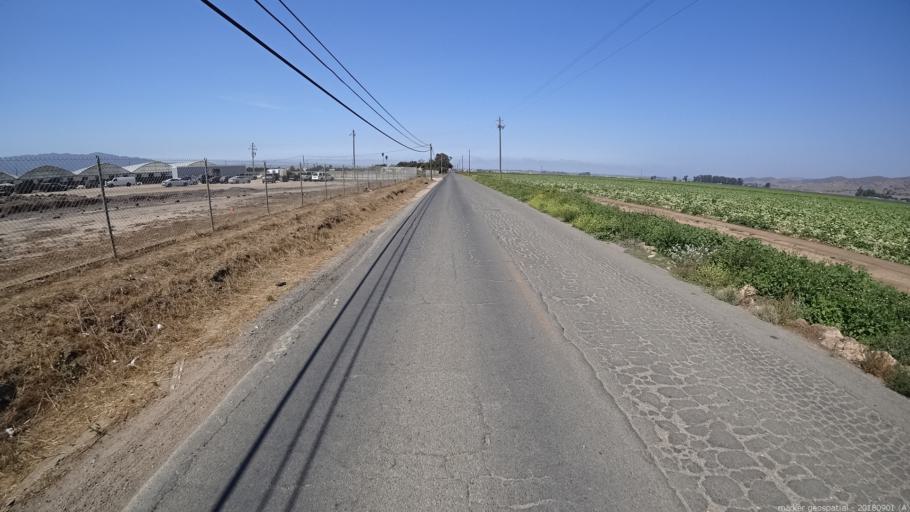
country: US
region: California
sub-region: Monterey County
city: Chualar
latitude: 36.6246
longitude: -121.5239
